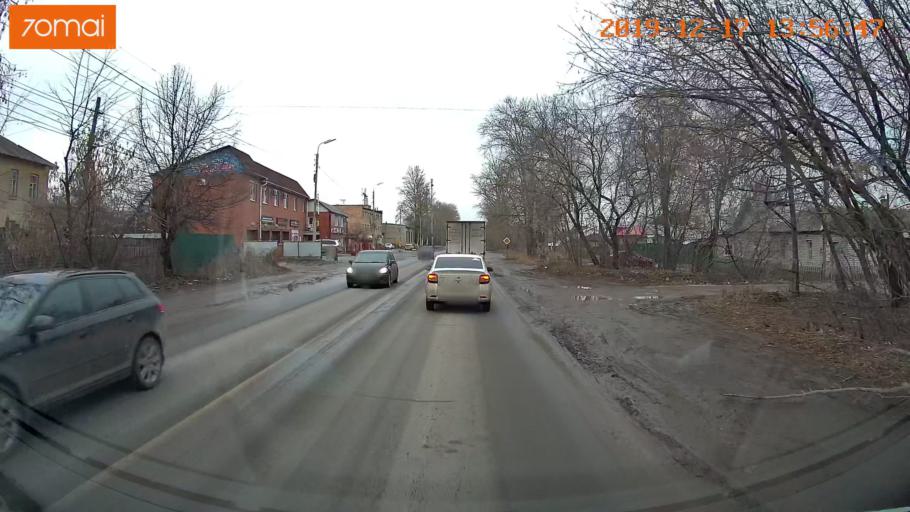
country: RU
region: Rjazan
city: Ryazan'
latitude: 54.6269
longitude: 39.6933
